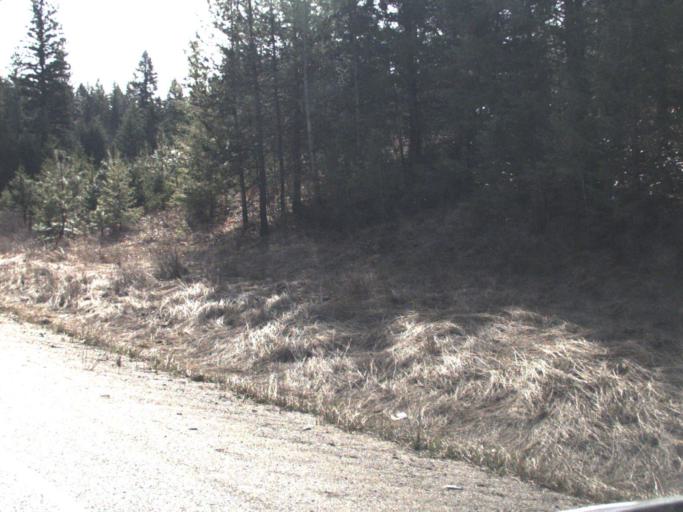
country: US
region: Washington
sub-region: Stevens County
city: Colville
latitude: 48.5399
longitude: -117.8282
